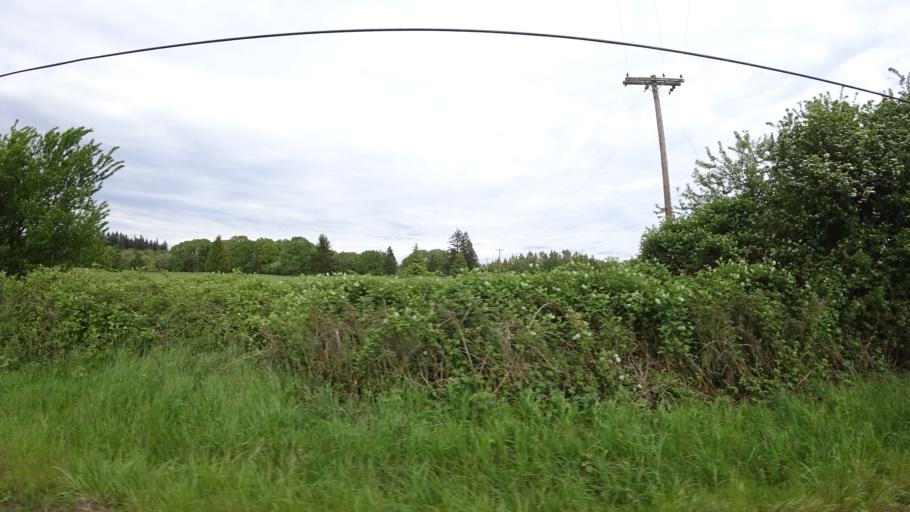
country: US
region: Oregon
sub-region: Washington County
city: Hillsboro
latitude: 45.4862
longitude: -122.9497
